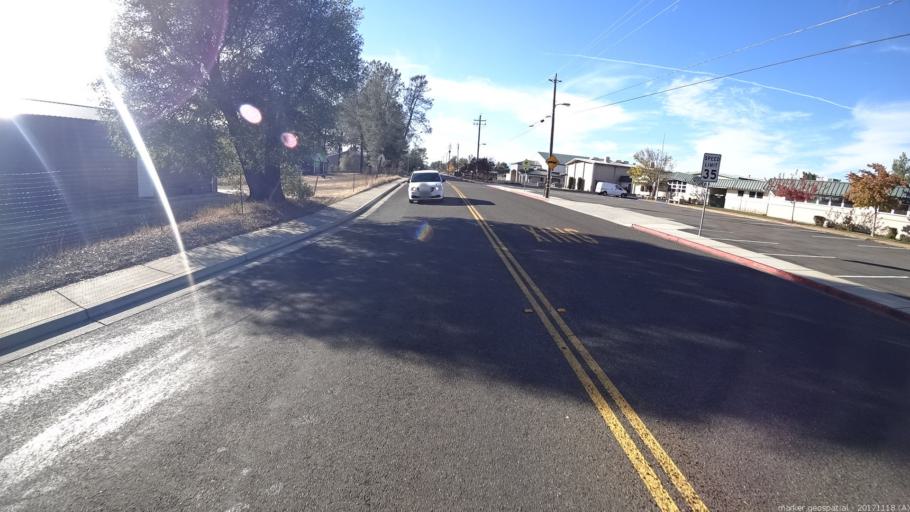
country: US
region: California
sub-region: Shasta County
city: Anderson
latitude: 40.4466
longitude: -122.4081
